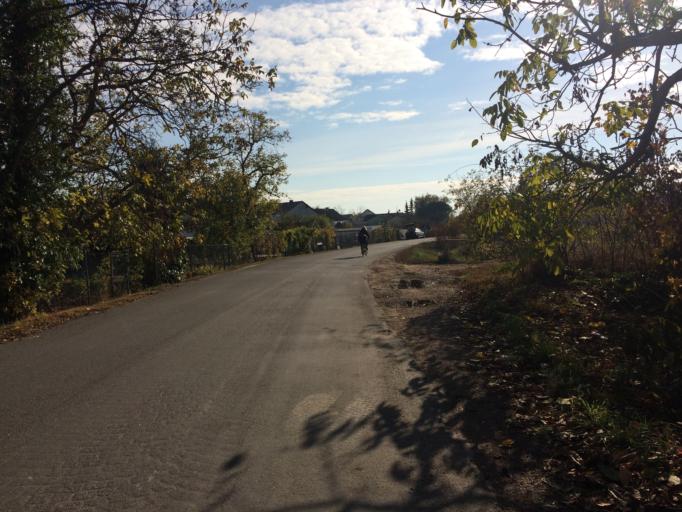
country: DE
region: Rheinland-Pfalz
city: Speyer
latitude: 49.3042
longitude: 8.4460
